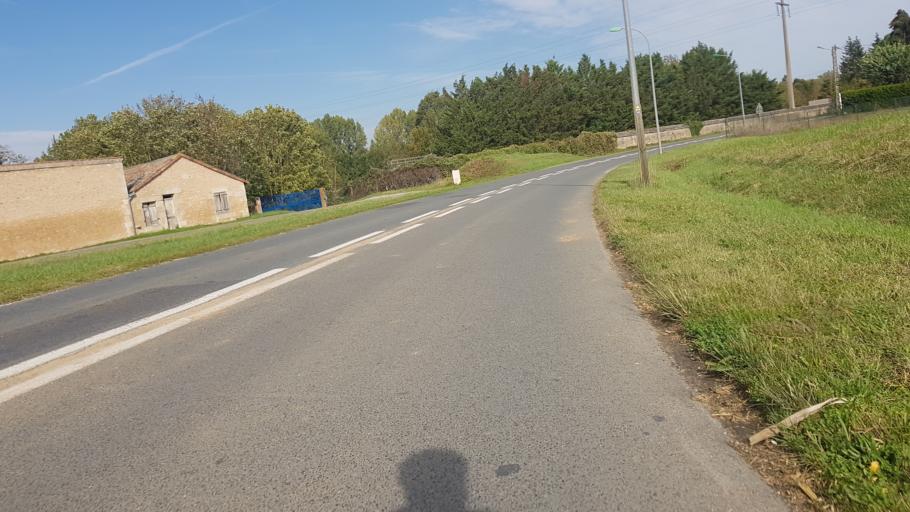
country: FR
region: Poitou-Charentes
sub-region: Departement de la Vienne
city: Chasseneuil-du-Poitou
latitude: 46.6273
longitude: 0.3665
